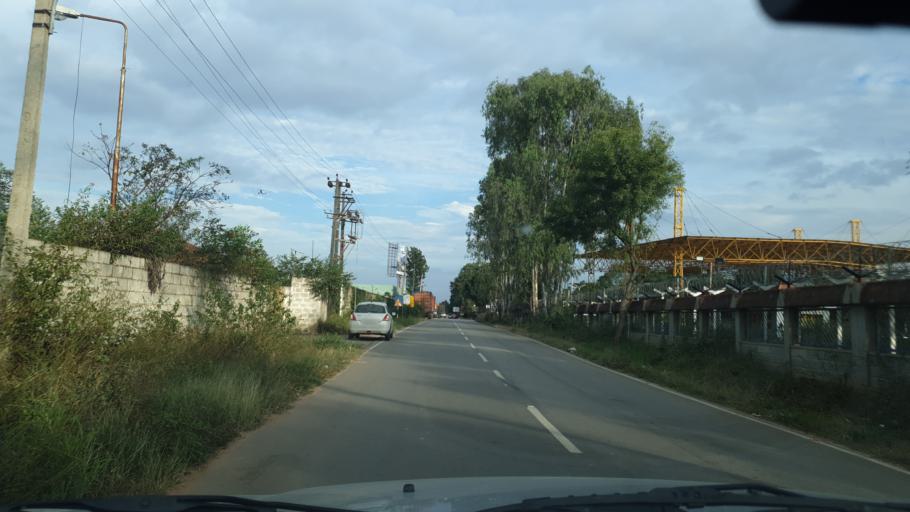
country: IN
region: Karnataka
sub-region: Bangalore Rural
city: Devanhalli
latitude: 13.1890
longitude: 77.6413
